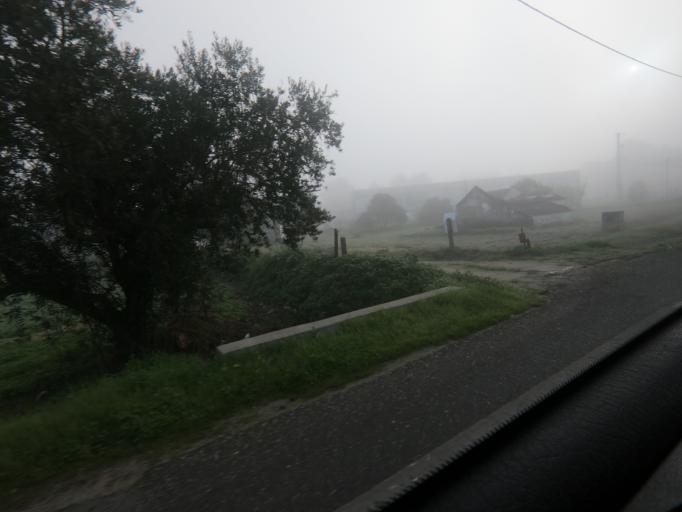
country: PT
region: Setubal
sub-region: Palmela
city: Pinhal Novo
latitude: 38.6149
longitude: -8.9124
